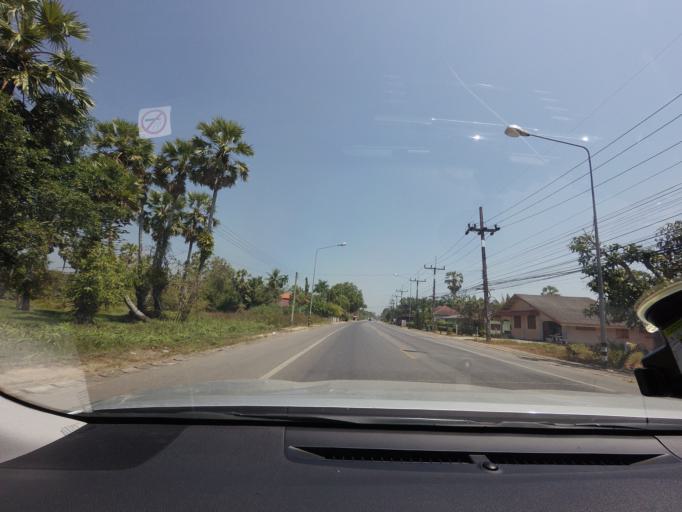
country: TH
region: Surat Thani
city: Tha Chang
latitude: 9.2439
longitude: 99.1830
